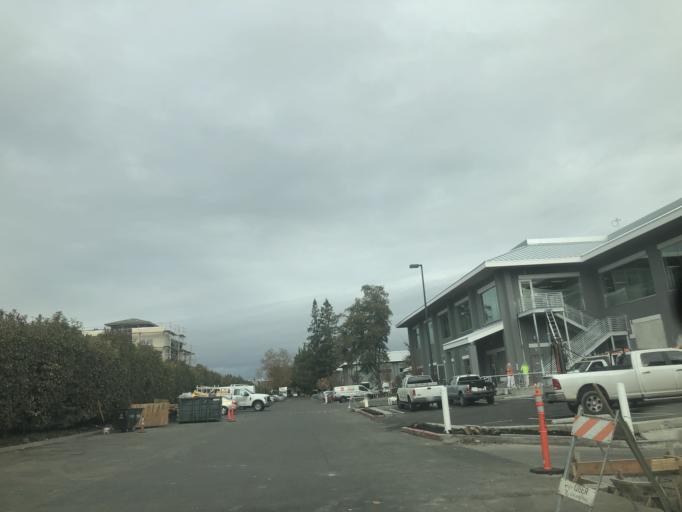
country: US
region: California
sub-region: Santa Clara County
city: Santa Clara
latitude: 37.3746
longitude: -121.9910
